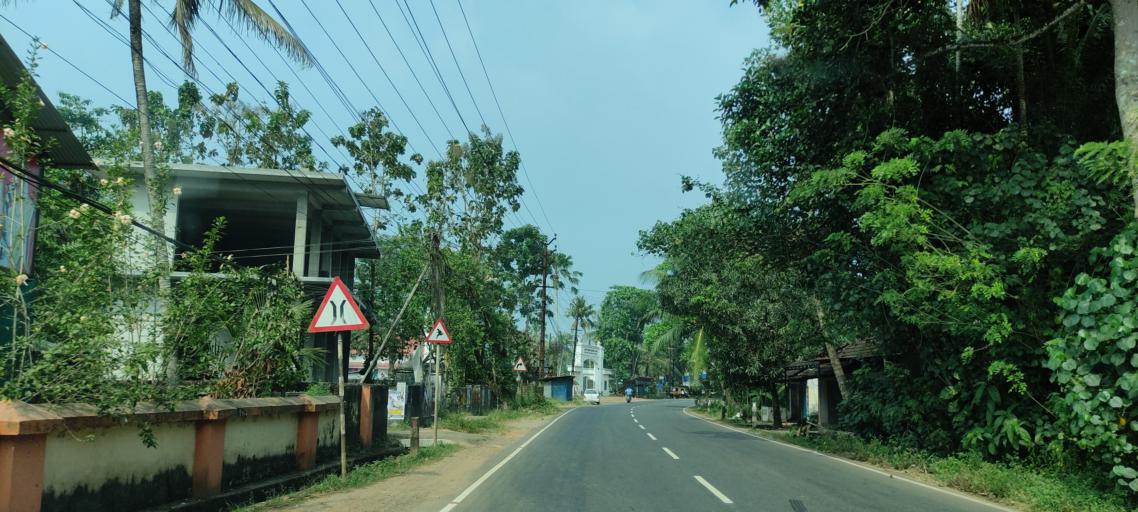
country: IN
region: Kerala
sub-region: Kottayam
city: Vaikam
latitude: 9.7659
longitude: 76.4150
